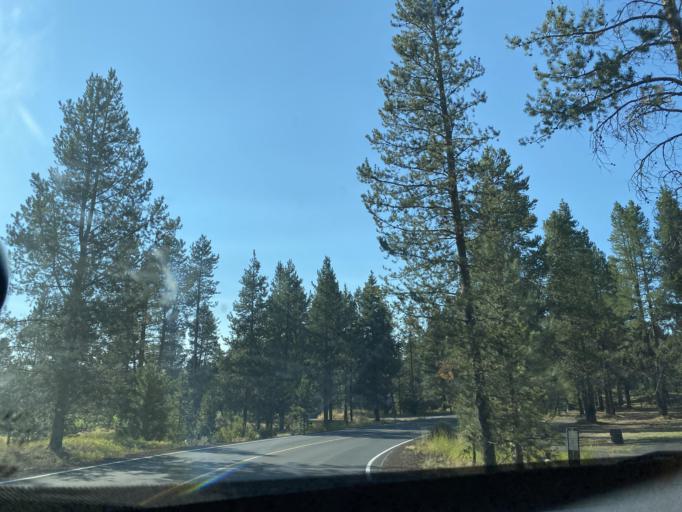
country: US
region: Oregon
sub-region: Deschutes County
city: Sunriver
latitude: 43.8800
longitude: -121.4373
